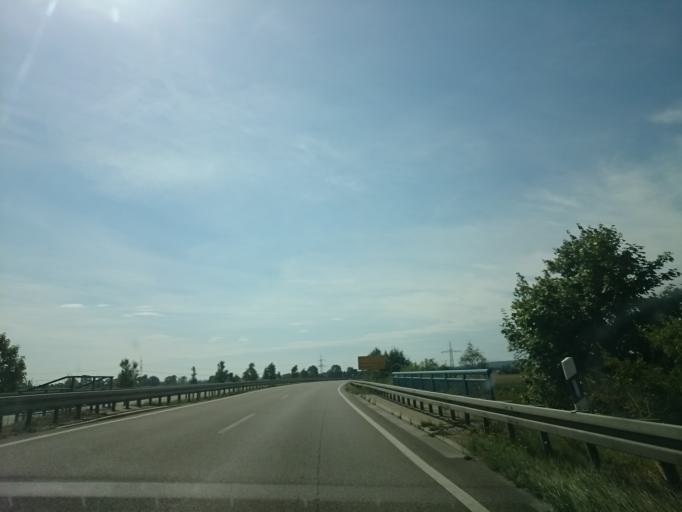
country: DE
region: Bavaria
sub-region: Swabia
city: Meitingen
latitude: 48.5441
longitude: 10.8427
